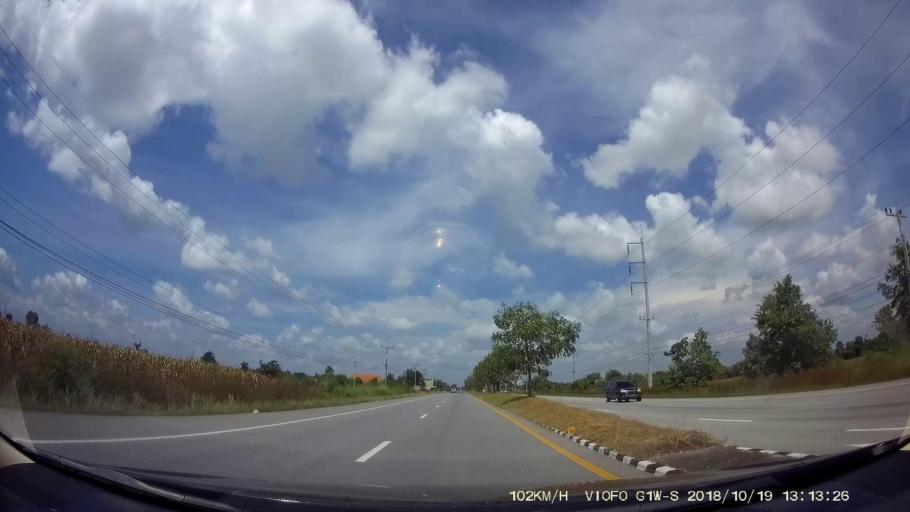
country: TH
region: Nakhon Ratchasima
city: Dan Khun Thot
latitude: 15.3597
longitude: 101.8295
